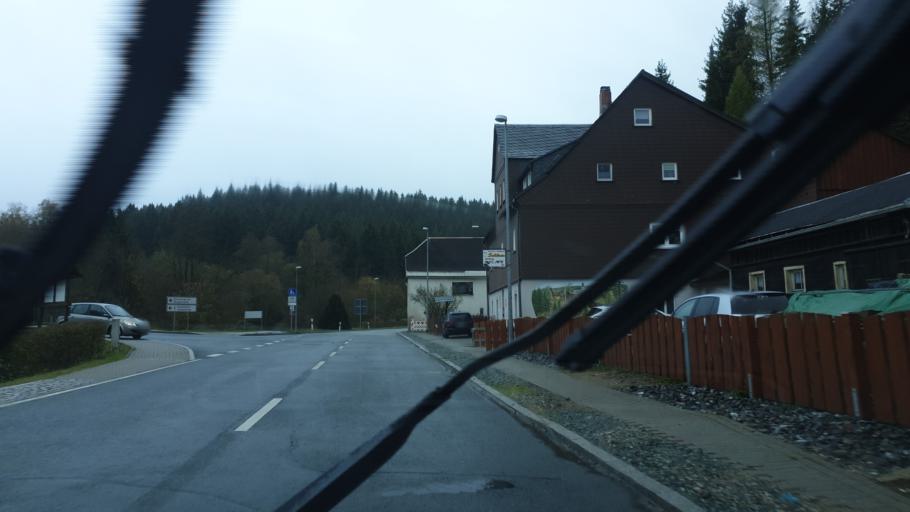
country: DE
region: Saxony
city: Muldenhammer
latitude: 50.4597
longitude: 12.4900
